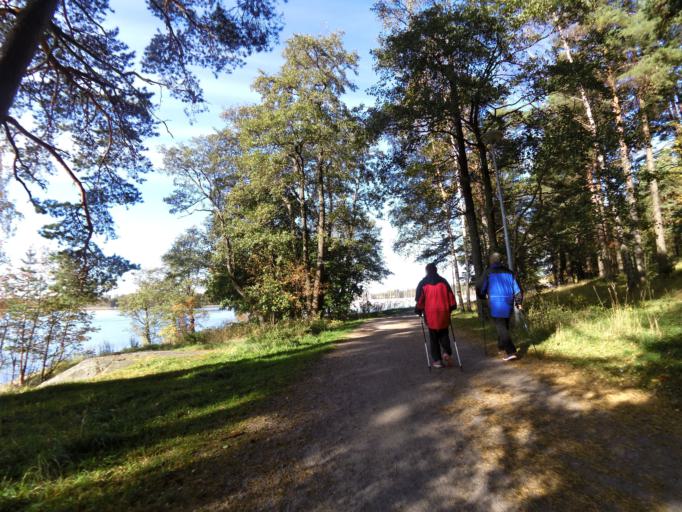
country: FI
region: Uusimaa
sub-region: Helsinki
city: Espoo
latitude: 60.1527
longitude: 24.6274
